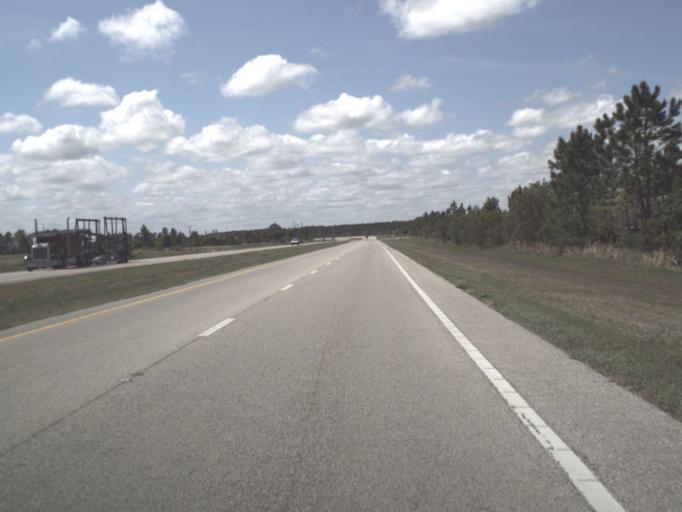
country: US
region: Florida
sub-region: Flagler County
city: Palm Coast
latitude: 29.6074
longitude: -81.2819
